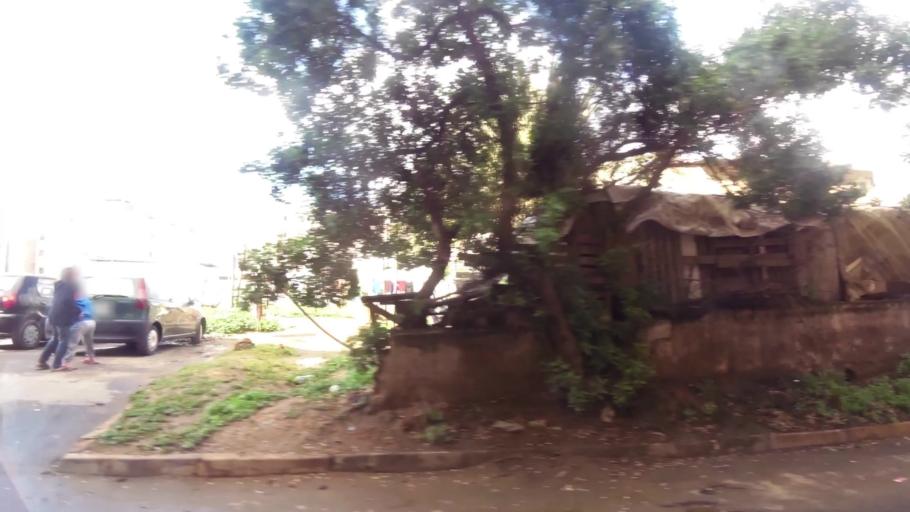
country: MA
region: Grand Casablanca
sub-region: Nouaceur
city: Bouskoura
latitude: 33.5323
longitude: -7.6849
